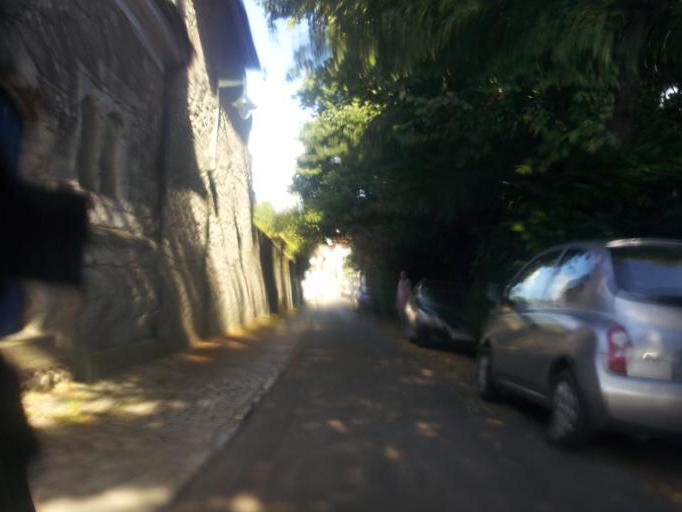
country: GB
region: England
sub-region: Kent
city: Headcorn
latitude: 51.2134
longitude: 0.5938
